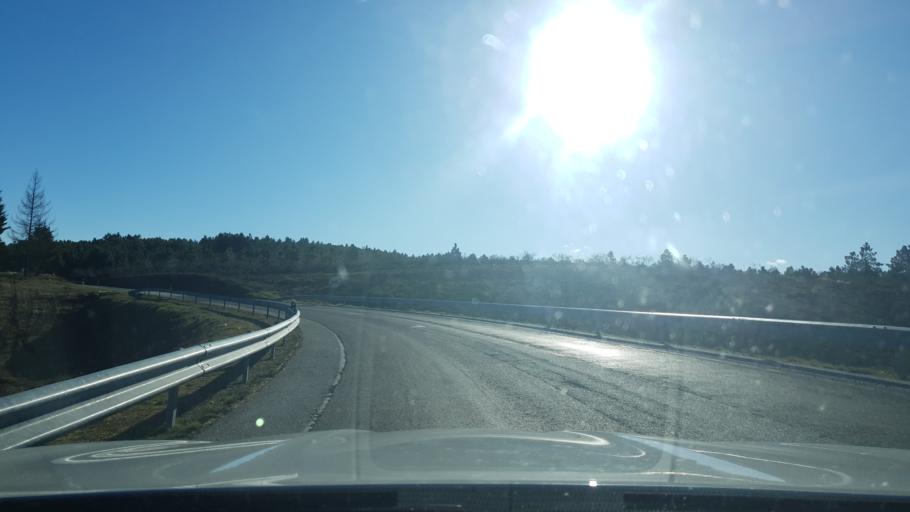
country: PT
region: Braganca
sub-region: Freixo de Espada A Cinta
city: Freixo de Espada a Cinta
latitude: 41.1640
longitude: -6.7990
